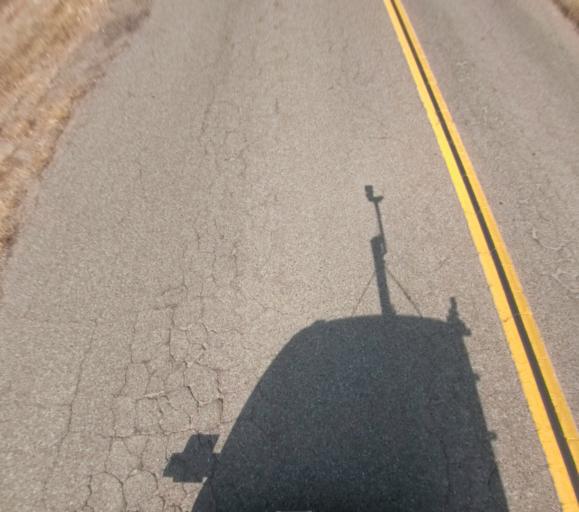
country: US
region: California
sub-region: Madera County
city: Oakhurst
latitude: 37.2402
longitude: -119.5307
